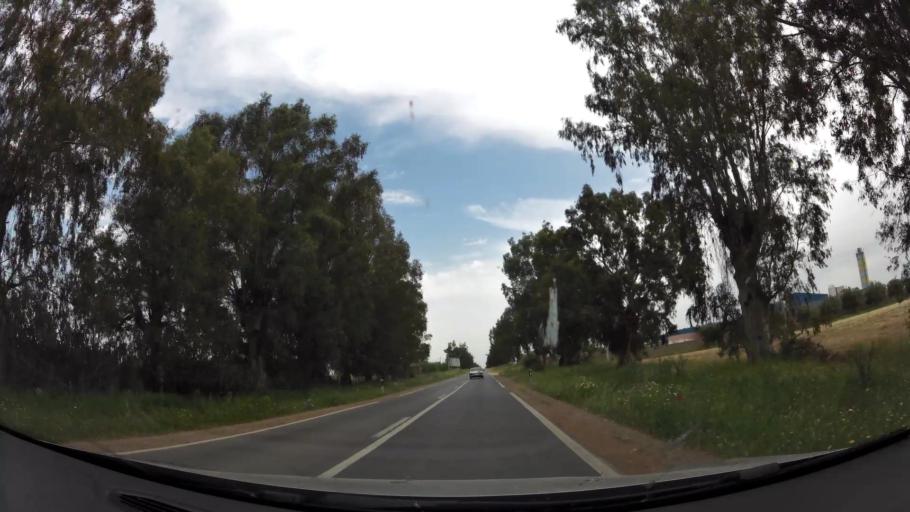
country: MA
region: Rabat-Sale-Zemmour-Zaer
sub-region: Khemisset
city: Tiflet
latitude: 33.8681
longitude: -6.2753
